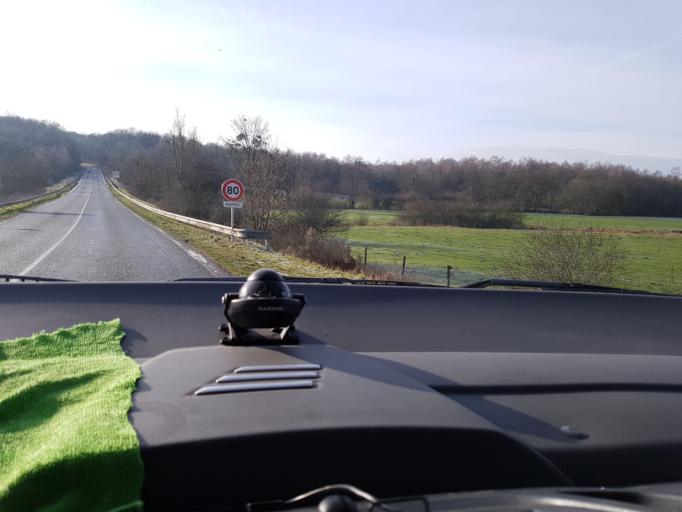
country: FR
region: Nord-Pas-de-Calais
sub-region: Departement du Nord
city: Sains-du-Nord
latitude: 50.0660
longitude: 4.0210
